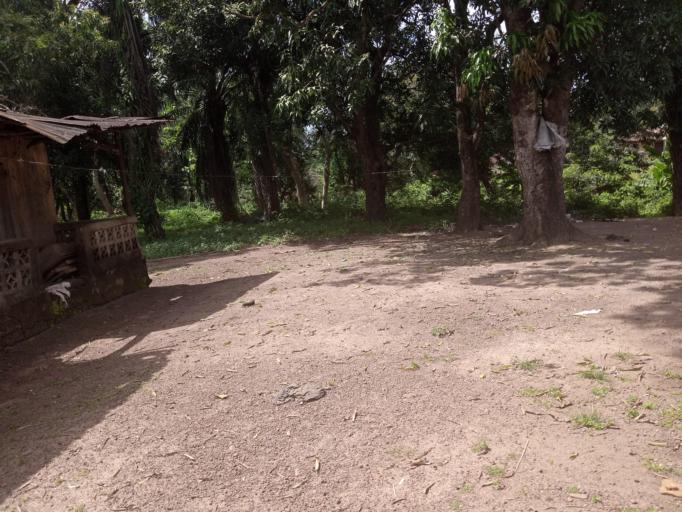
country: SL
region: Northern Province
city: Kamakwie
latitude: 9.4957
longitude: -12.2448
